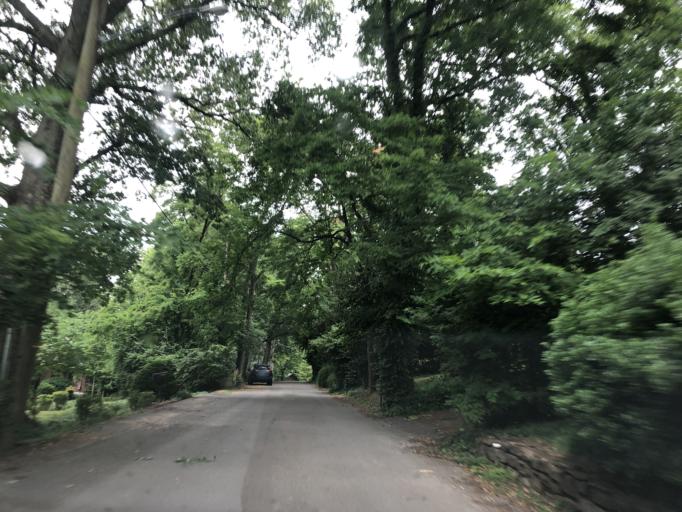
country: US
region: Tennessee
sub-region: Davidson County
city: Nashville
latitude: 36.1332
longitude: -86.8135
